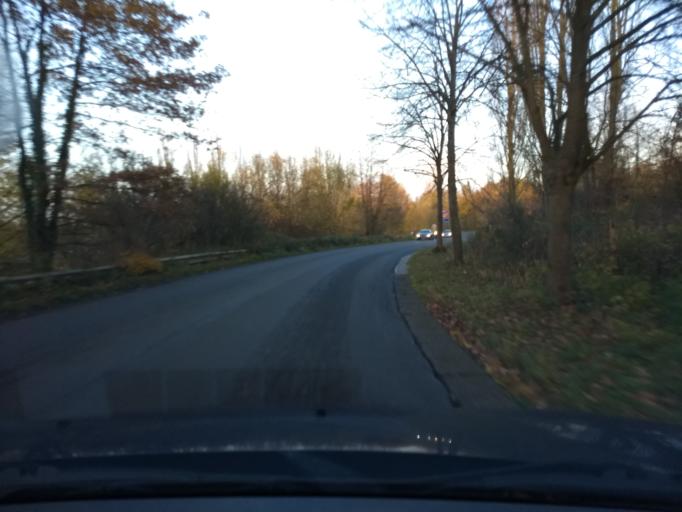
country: BE
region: Wallonia
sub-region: Province du Brabant Wallon
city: Ittre
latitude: 50.6157
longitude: 4.2270
